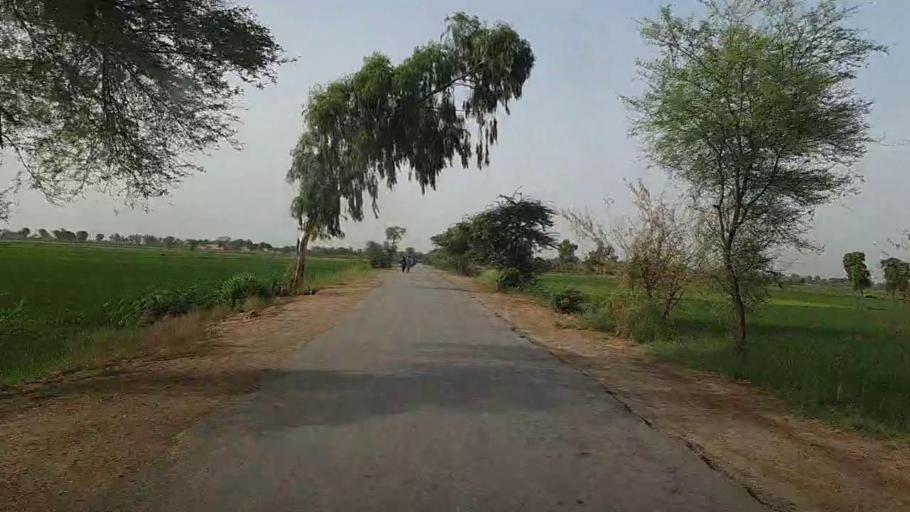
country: PK
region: Sindh
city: Khairpur Nathan Shah
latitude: 27.1240
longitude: 67.7894
